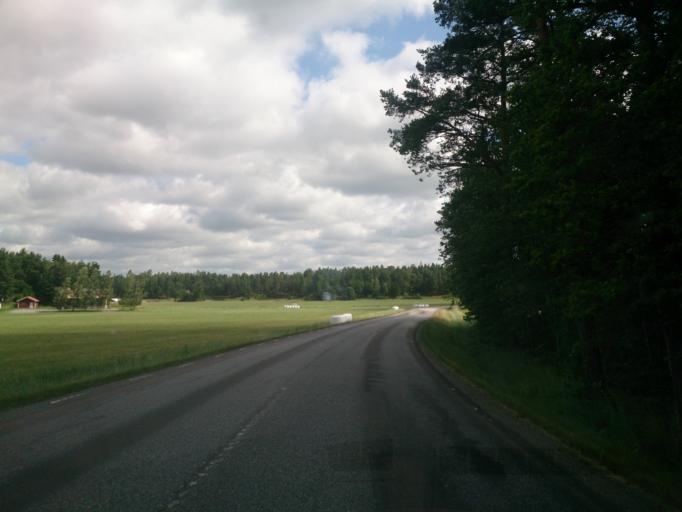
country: SE
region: OEstergoetland
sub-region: Norrkopings Kommun
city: Kimstad
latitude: 58.4817
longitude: 15.9491
